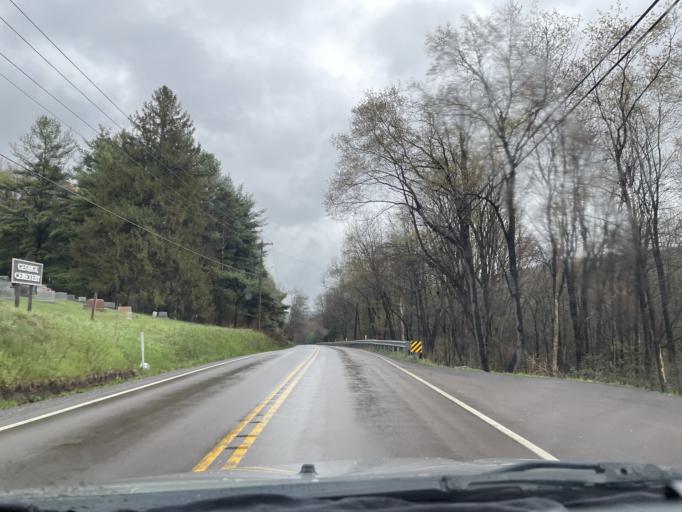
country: US
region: Maryland
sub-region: Garrett County
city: Mountain Lake Park
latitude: 39.4552
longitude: -79.2510
